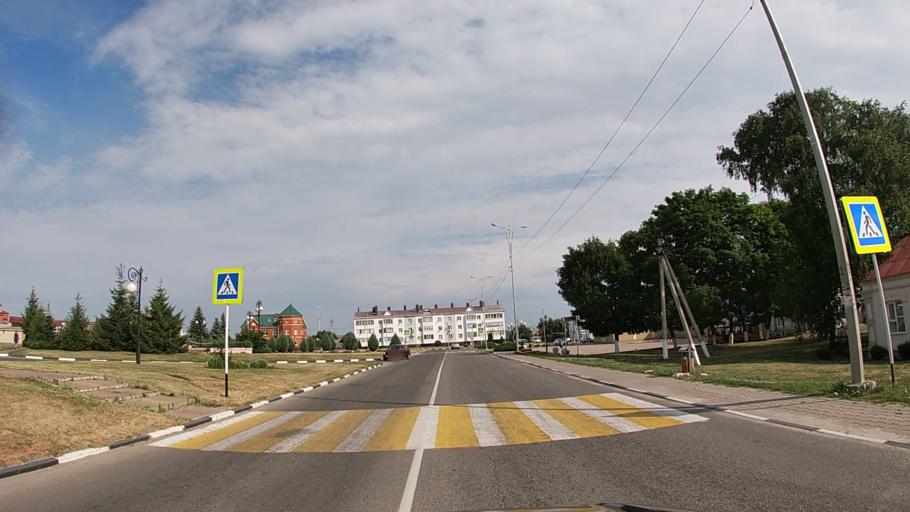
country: RU
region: Belgorod
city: Krasnaya Yaruga
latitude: 50.8015
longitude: 35.6600
